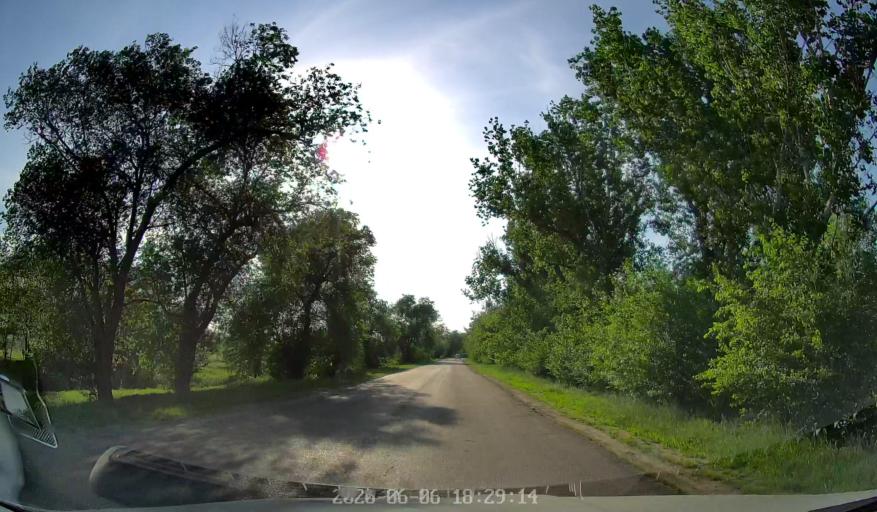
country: MD
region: Chisinau
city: Ciorescu
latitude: 47.1317
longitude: 28.9728
